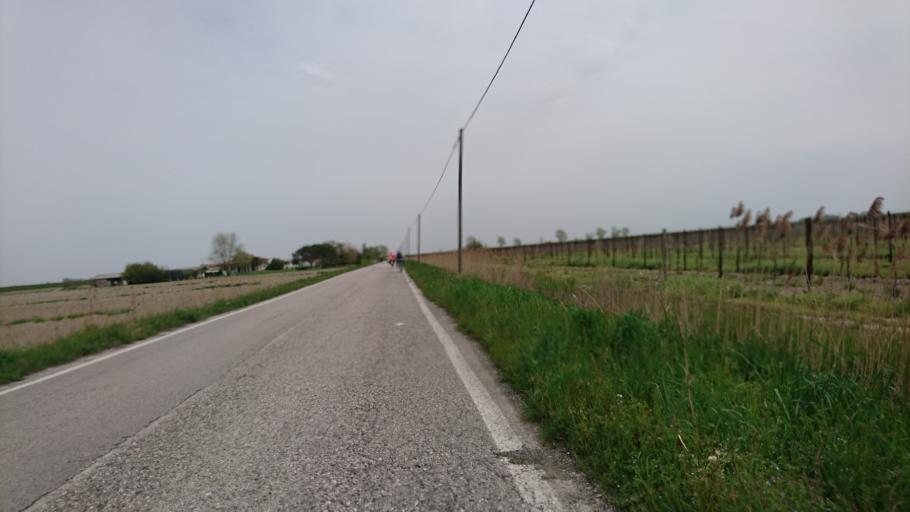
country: IT
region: Veneto
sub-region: Provincia di Venezia
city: La Salute di Livenza
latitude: 45.6684
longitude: 12.8471
